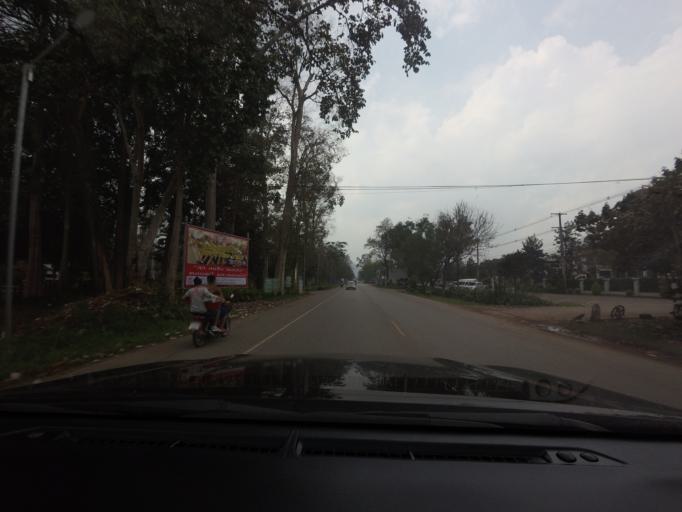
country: TH
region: Nakhon Ratchasima
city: Pak Chong
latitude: 14.5347
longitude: 101.3796
